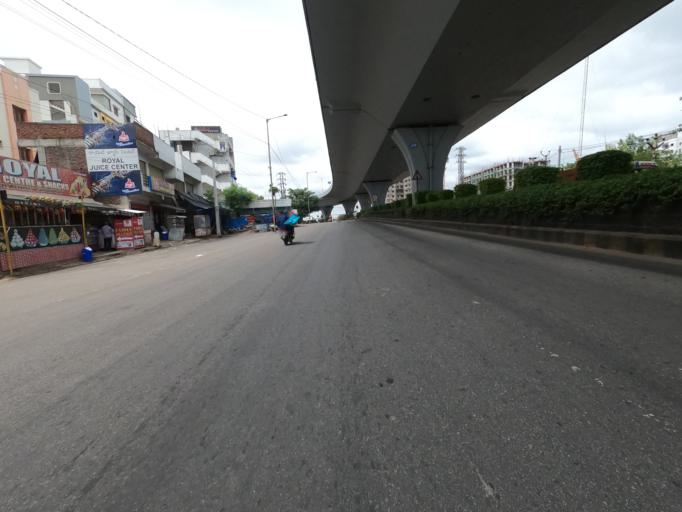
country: IN
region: Telangana
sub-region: Hyderabad
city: Hyderabad
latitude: 17.3279
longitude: 78.4256
